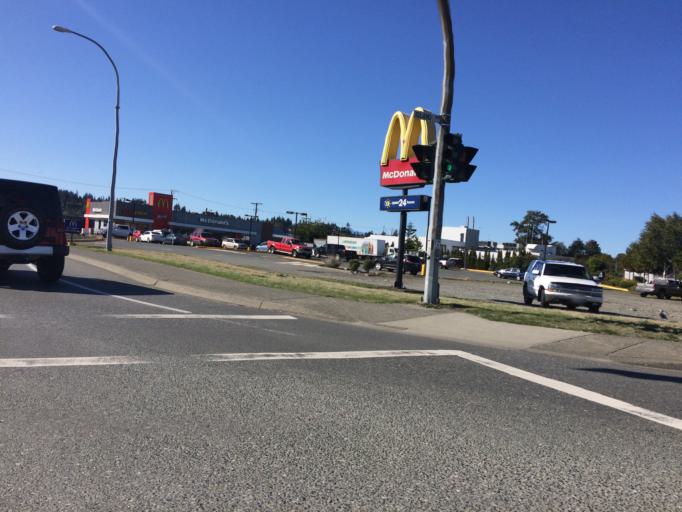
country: CA
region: British Columbia
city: Campbell River
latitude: 50.0304
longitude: -125.2453
